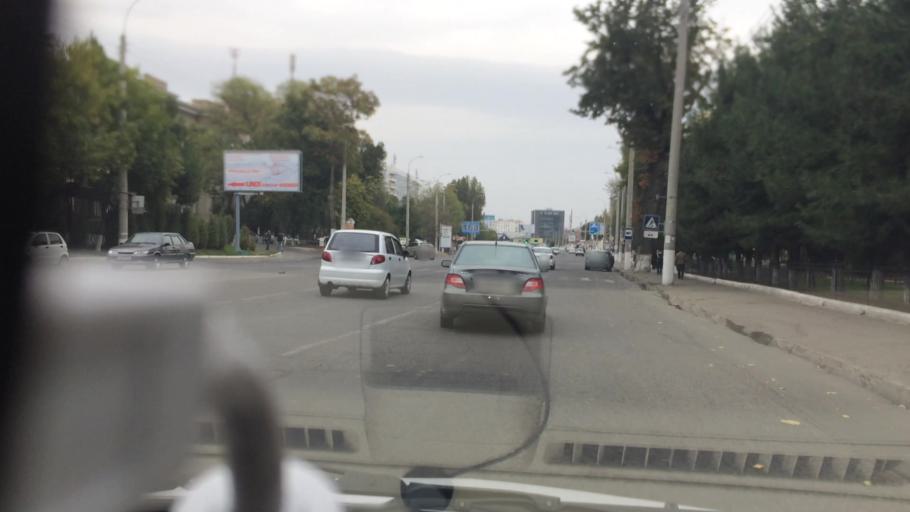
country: UZ
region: Toshkent
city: Salor
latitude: 41.3181
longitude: 69.3136
